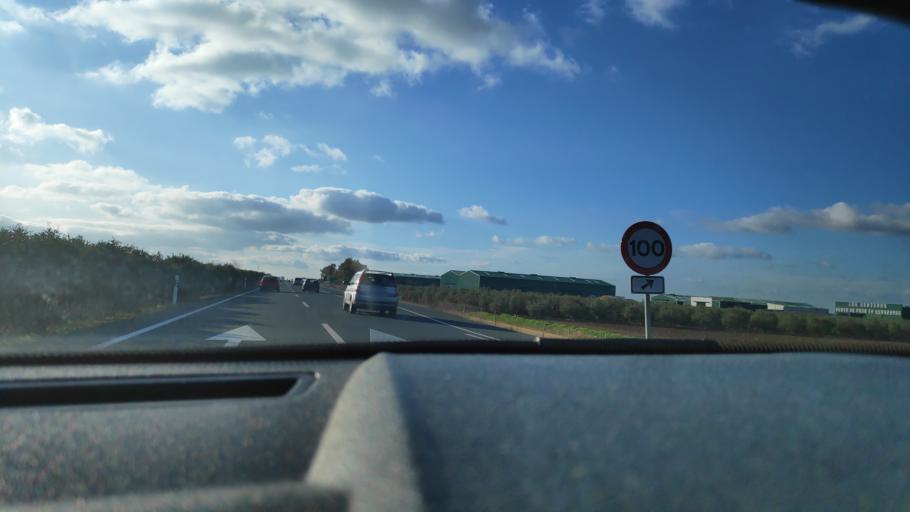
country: ES
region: Andalusia
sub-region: Provincia de Sevilla
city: La Campana
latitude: 37.5085
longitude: -5.4209
